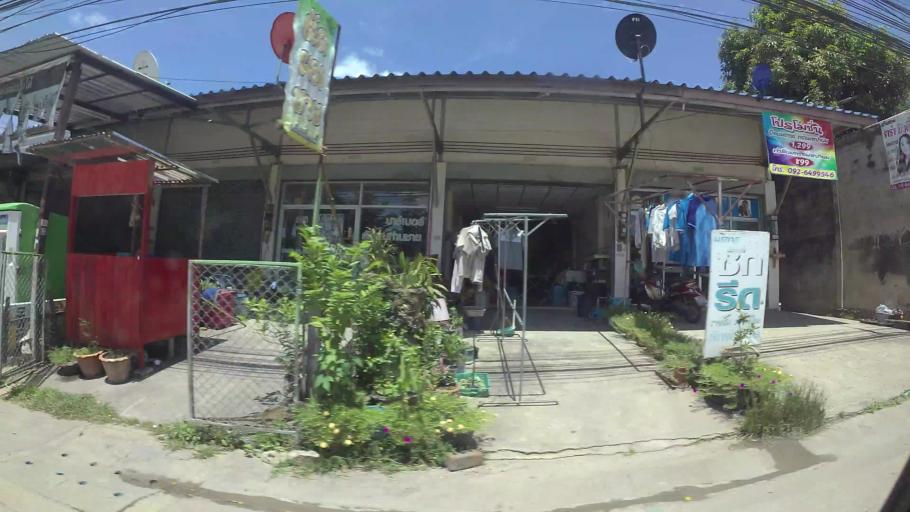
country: TH
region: Chon Buri
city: Ban Talat Bueng
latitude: 13.1147
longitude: 100.9592
